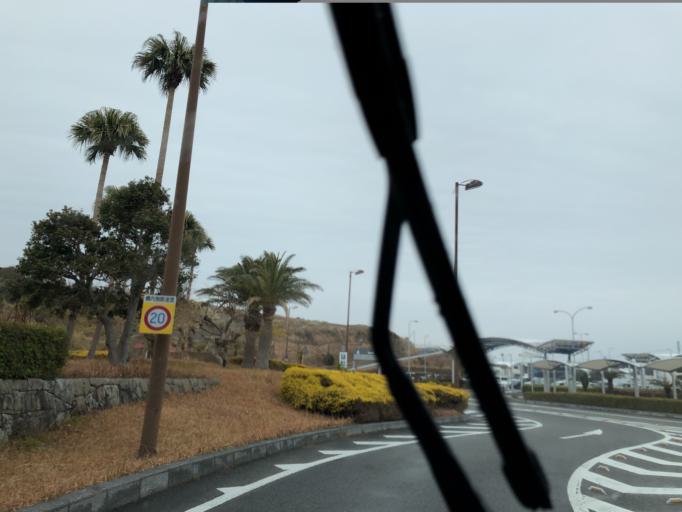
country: JP
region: Wakayama
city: Tanabe
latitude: 33.6625
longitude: 135.3595
